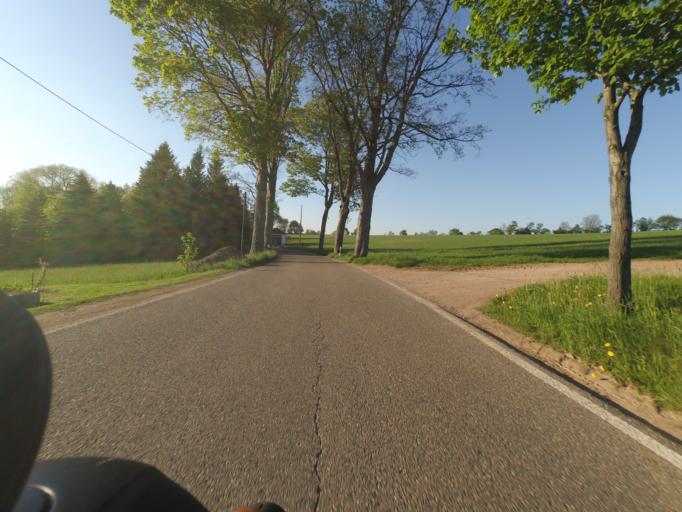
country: DE
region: Saxony
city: Altenberg
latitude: 50.8129
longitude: 13.7388
